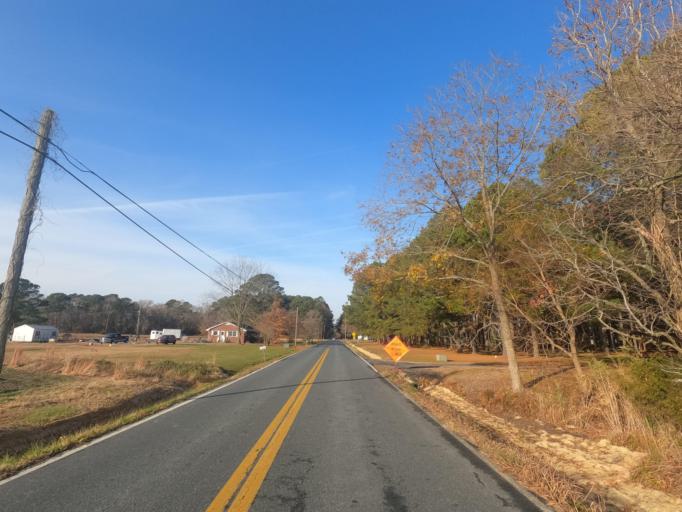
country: US
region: Maryland
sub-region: Somerset County
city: Crisfield
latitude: 38.0334
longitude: -75.7825
